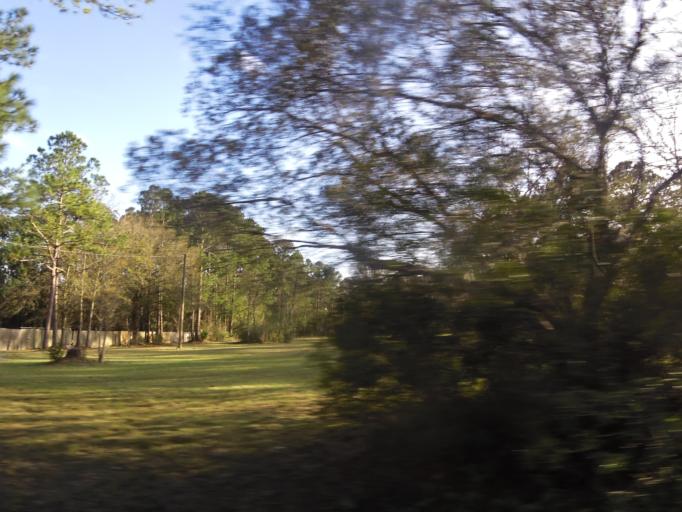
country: US
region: Florida
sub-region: Duval County
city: Jacksonville
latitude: 30.2679
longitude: -81.5793
